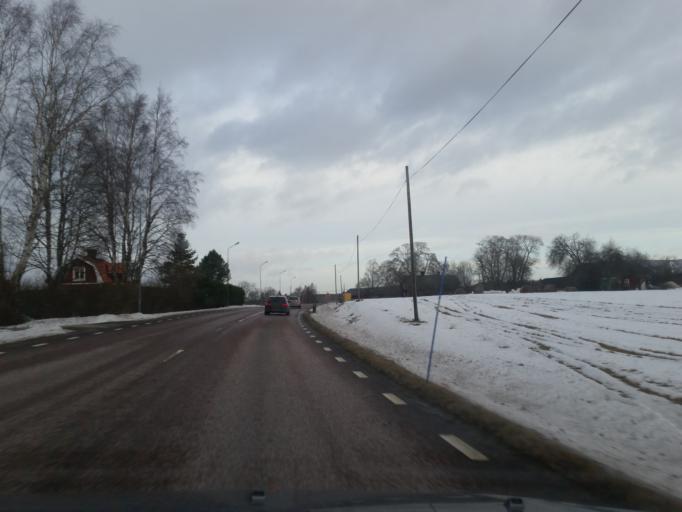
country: SE
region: Gaevleborg
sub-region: Sandvikens Kommun
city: Jarbo
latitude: 60.6730
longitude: 16.6699
